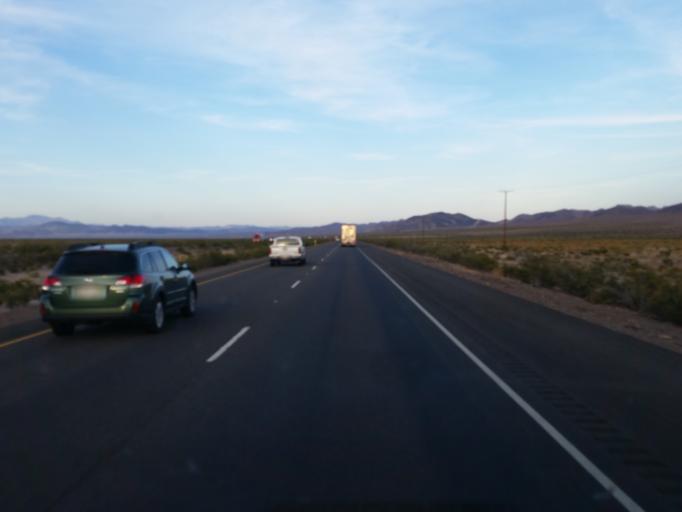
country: US
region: California
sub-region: San Bernardino County
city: Joshua Tree
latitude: 34.7337
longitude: -116.2911
